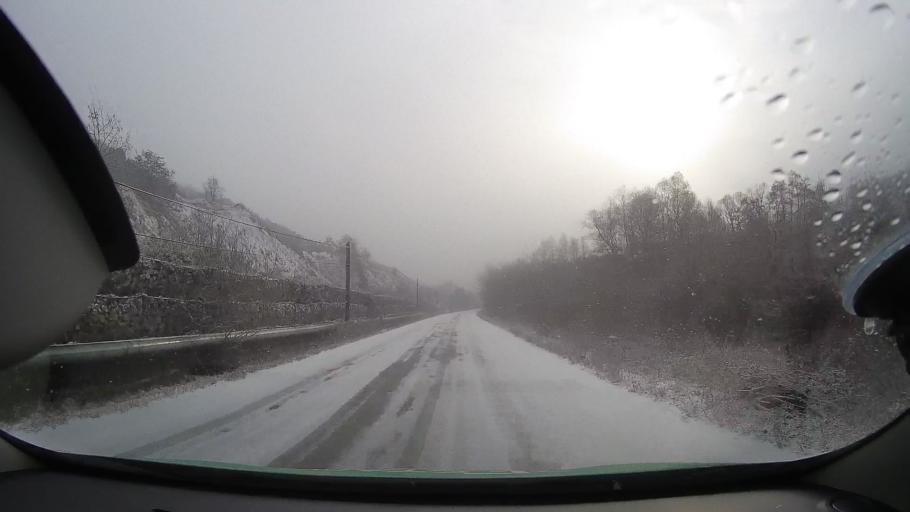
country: RO
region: Alba
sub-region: Comuna Livezile
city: Livezile
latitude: 46.3593
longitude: 23.6127
